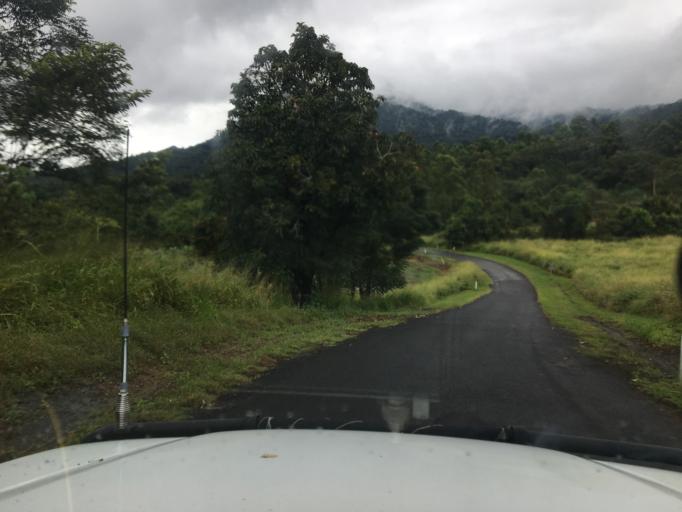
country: AU
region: Queensland
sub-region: Cassowary Coast
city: Innisfail
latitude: -17.4477
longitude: 145.8575
